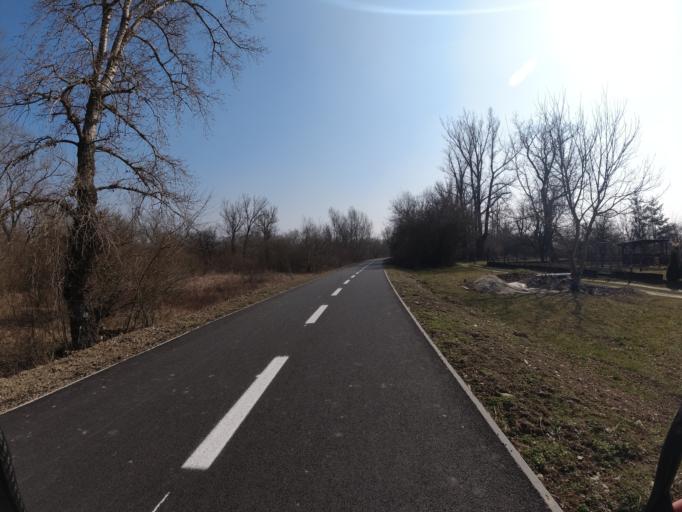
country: SK
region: Trenciansky
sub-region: Okres Nove Mesto nad Vahom
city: Nove Mesto nad Vahom
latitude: 48.7491
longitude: 17.8506
